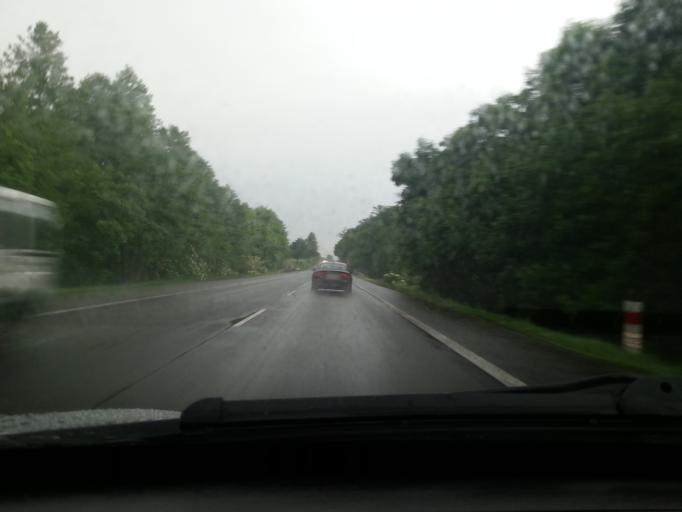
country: PL
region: Lodz Voivodeship
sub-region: Powiat zgierski
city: Strykow
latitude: 51.8705
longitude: 19.5726
